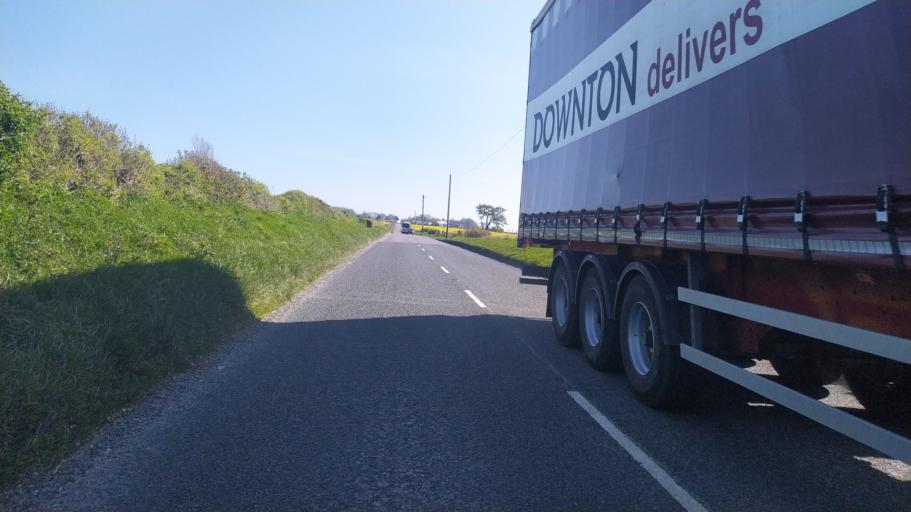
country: GB
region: England
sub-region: Wiltshire
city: Bishopstone
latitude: 51.0061
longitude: -1.8851
